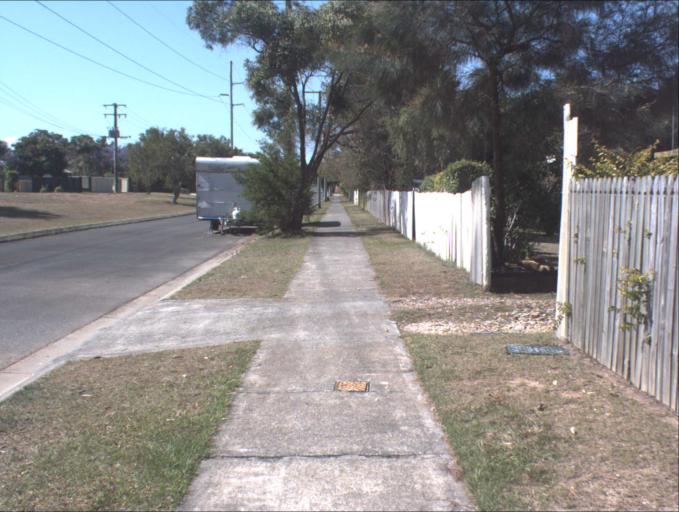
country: AU
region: Queensland
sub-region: Logan
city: Beenleigh
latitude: -27.6971
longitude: 153.2094
